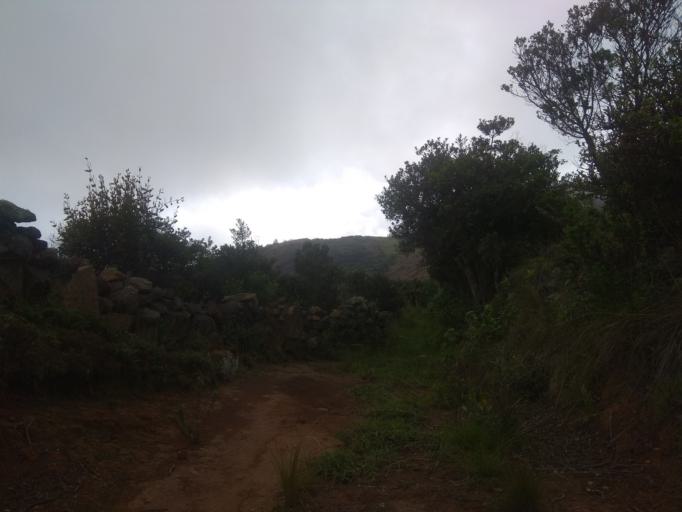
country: CO
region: Boyaca
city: Socha Viejo
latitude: 6.0078
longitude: -72.6787
